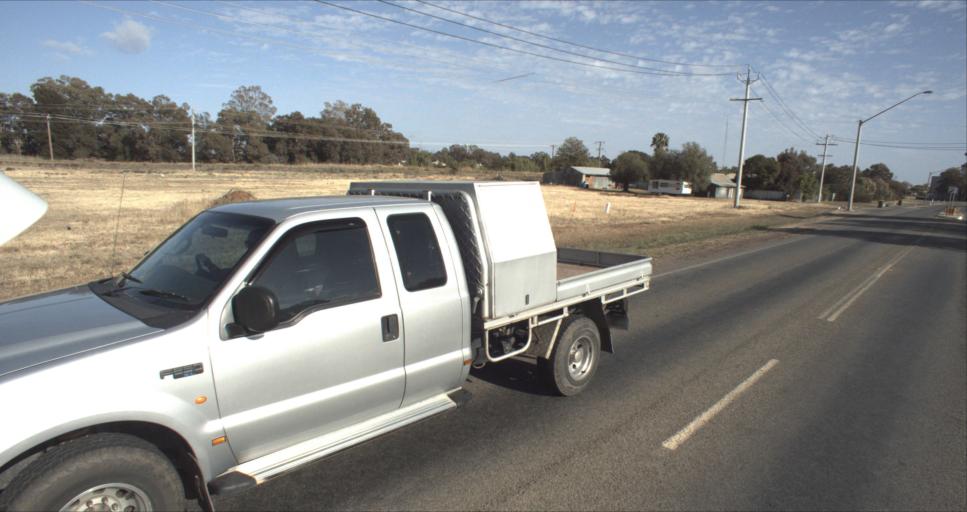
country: AU
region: New South Wales
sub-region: Leeton
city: Leeton
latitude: -34.5624
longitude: 146.3927
